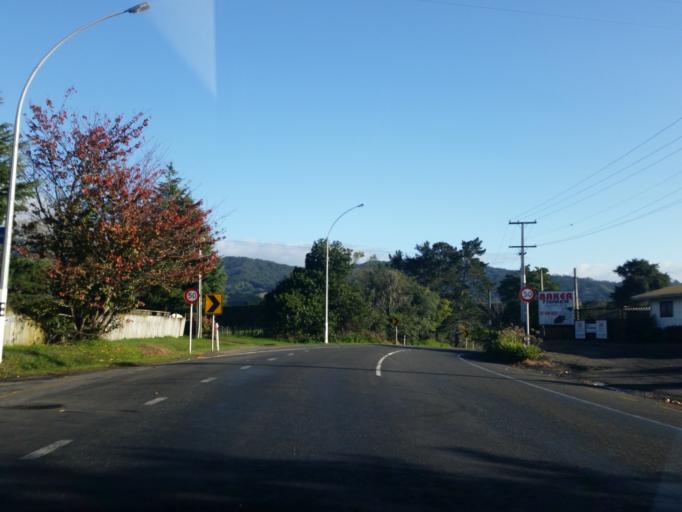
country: NZ
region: Bay of Plenty
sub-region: Western Bay of Plenty District
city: Katikati
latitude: -37.5480
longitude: 175.9113
